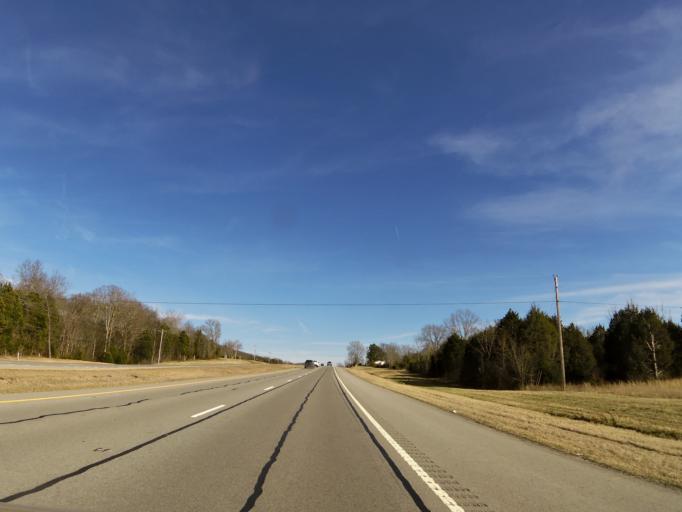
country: US
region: Tennessee
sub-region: Cannon County
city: Woodbury
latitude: 35.8154
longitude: -86.2234
